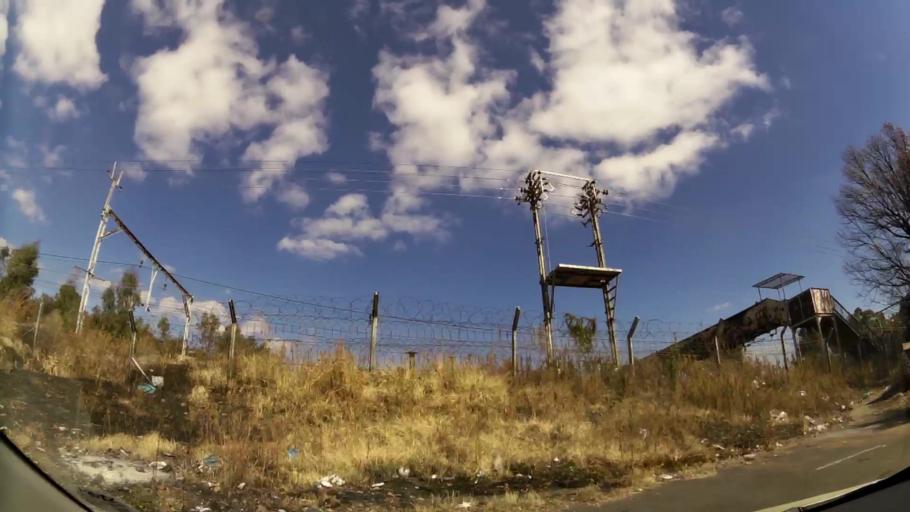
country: ZA
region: Gauteng
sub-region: West Rand District Municipality
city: Krugersdorp
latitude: -26.1098
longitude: 27.7823
